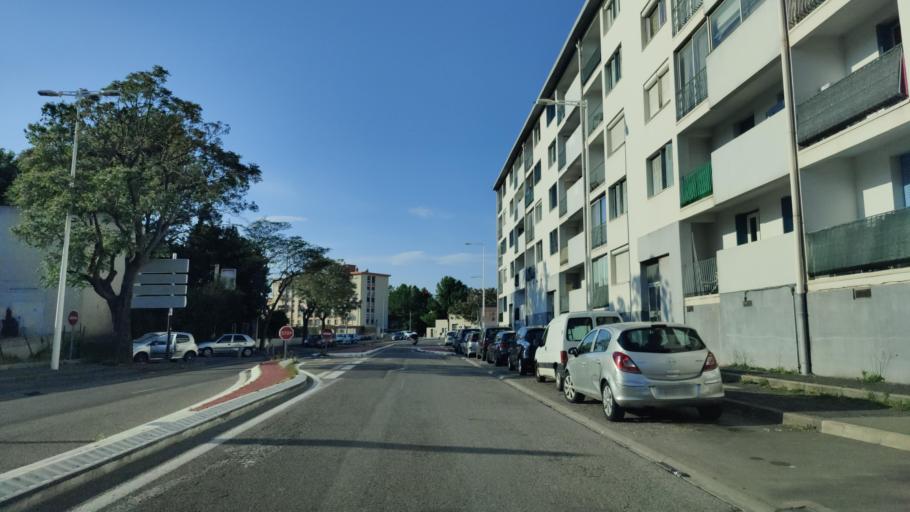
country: FR
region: Languedoc-Roussillon
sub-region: Departement des Pyrenees-Orientales
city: Perpignan
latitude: 42.7113
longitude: 2.8846
